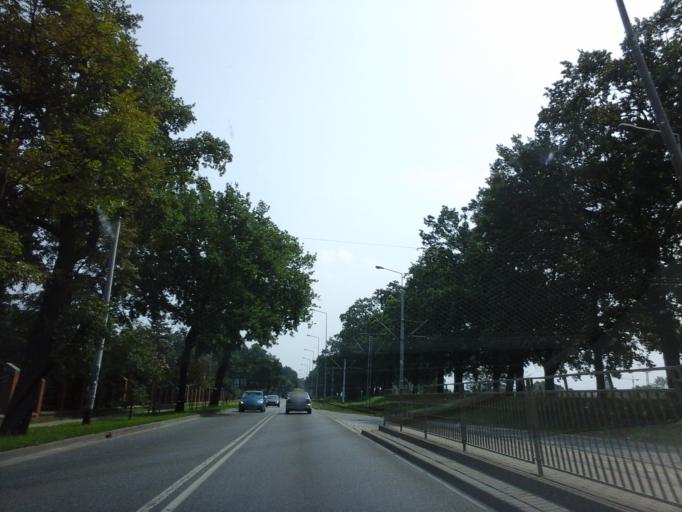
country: PL
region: Lower Silesian Voivodeship
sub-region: Powiat wroclawski
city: Wroclaw
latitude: 51.1346
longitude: 17.0115
